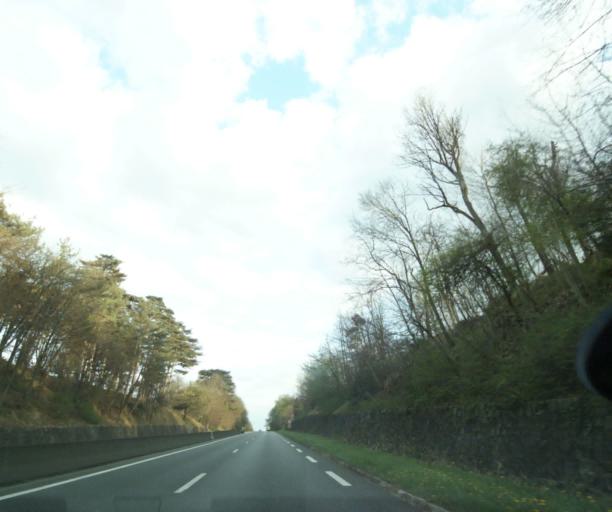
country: FR
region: Ile-de-France
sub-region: Departement de Seine-et-Marne
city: Barbizon
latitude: 48.4388
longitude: 2.6529
